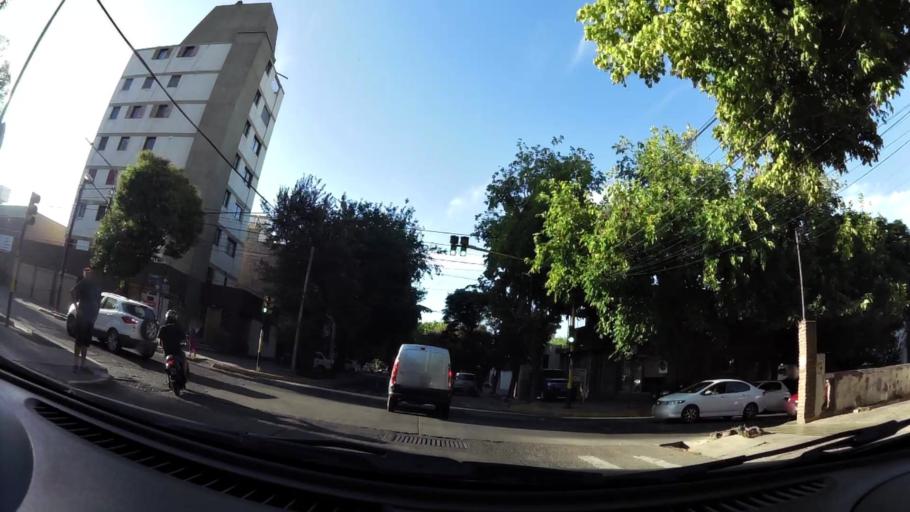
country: AR
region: Mendoza
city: Mendoza
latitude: -32.9048
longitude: -68.8516
